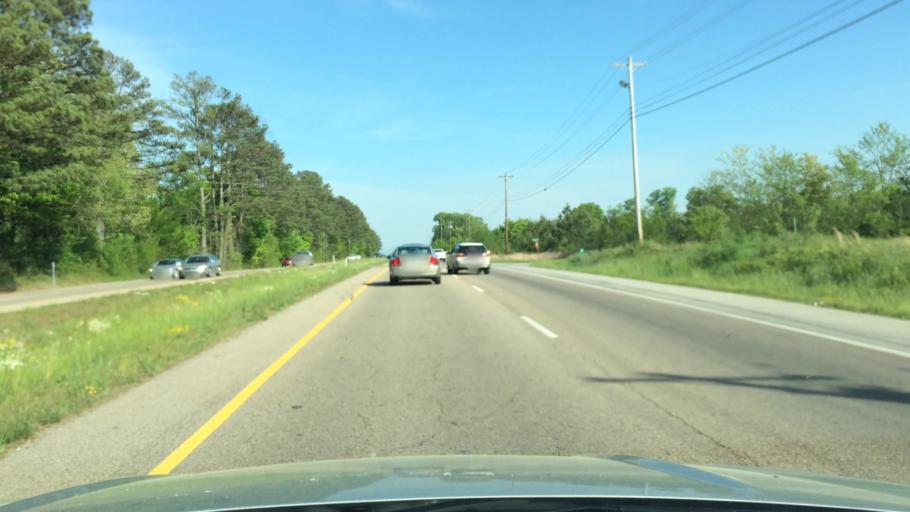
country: US
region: Tennessee
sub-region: Loudon County
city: Lenoir City
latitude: 35.8352
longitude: -84.2900
